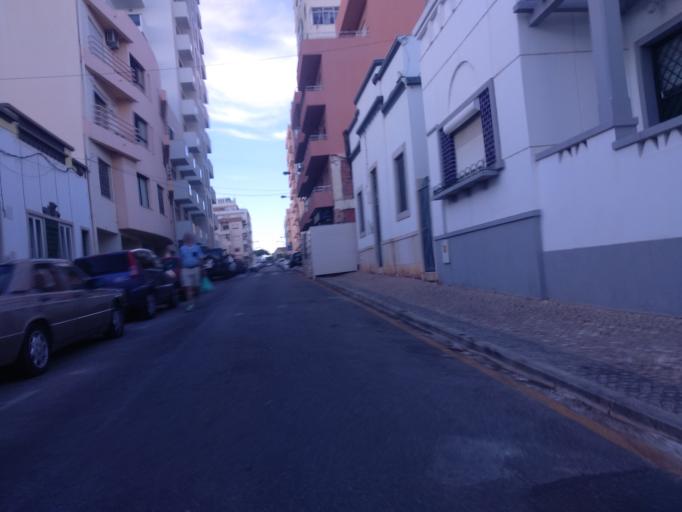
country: PT
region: Faro
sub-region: Faro
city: Faro
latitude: 37.0172
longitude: -7.9250
